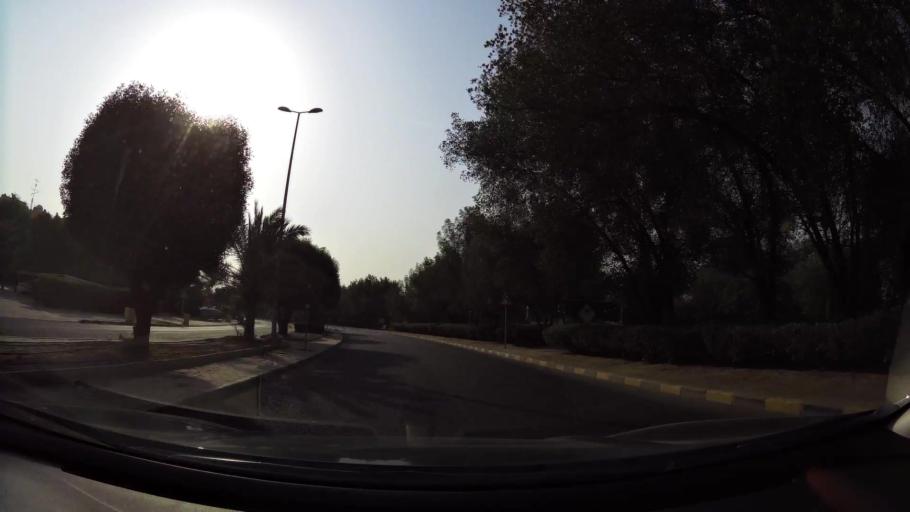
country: KW
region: Mubarak al Kabir
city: Sabah as Salim
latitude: 29.2677
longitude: 48.0668
